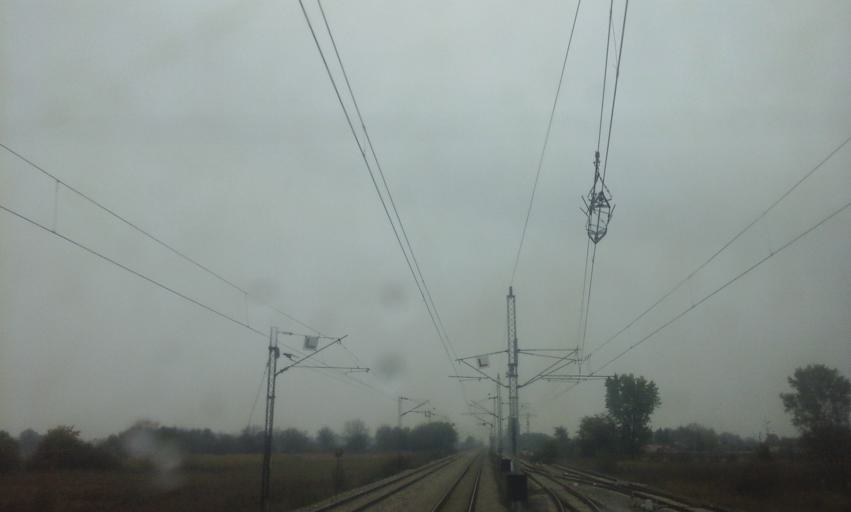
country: RS
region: Central Serbia
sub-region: Pomoravski Okrug
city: Paracin
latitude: 43.8717
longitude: 21.3939
